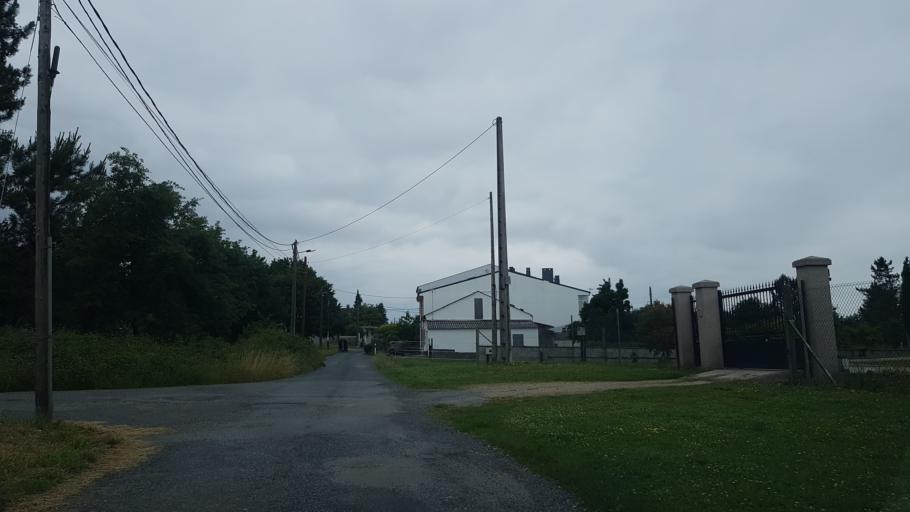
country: ES
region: Galicia
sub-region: Provincia de Lugo
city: Lugo
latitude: 43.0278
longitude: -7.5469
